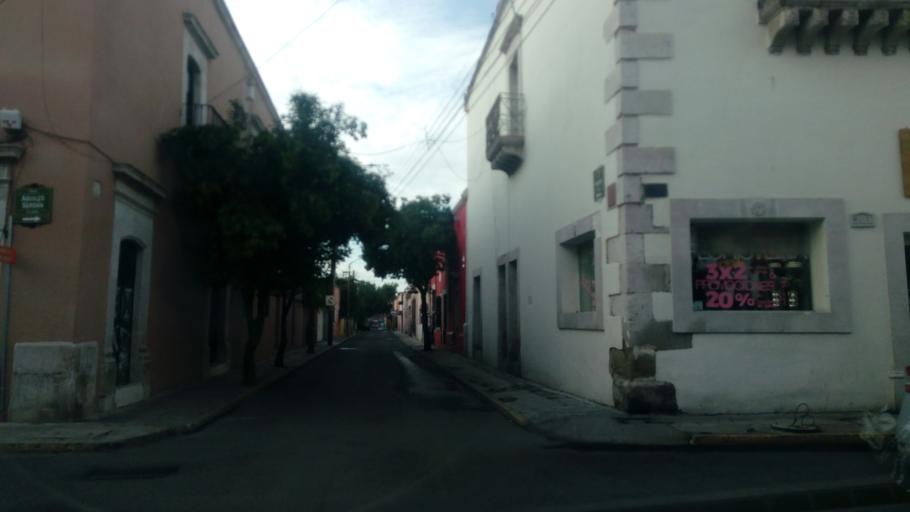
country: MX
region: Durango
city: Victoria de Durango
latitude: 24.0273
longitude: -104.6682
